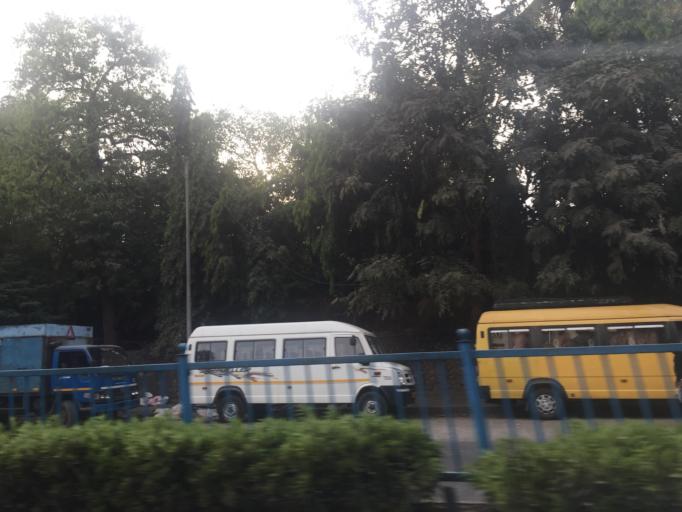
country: IN
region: Maharashtra
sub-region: Mumbai Suburban
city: Powai
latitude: 19.1231
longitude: 72.9254
